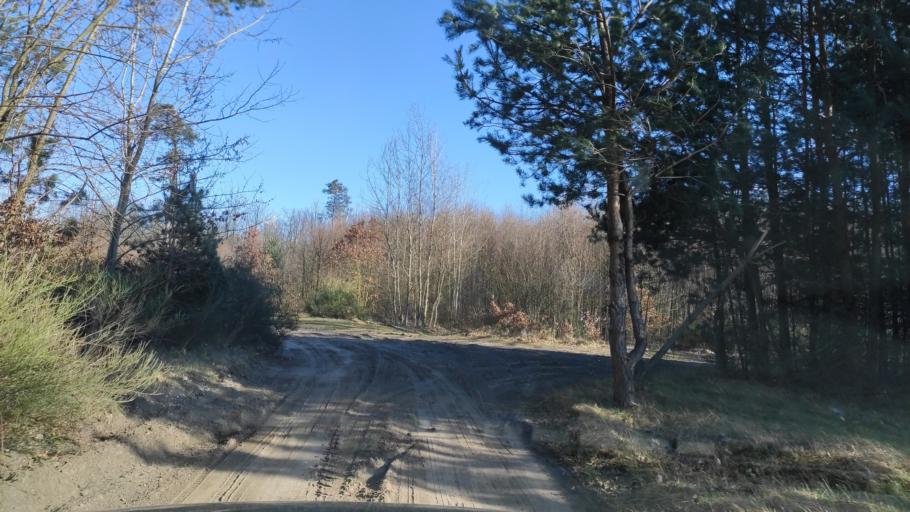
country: PL
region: Masovian Voivodeship
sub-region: Powiat radomski
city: Jedlnia-Letnisko
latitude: 51.4525
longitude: 21.2826
